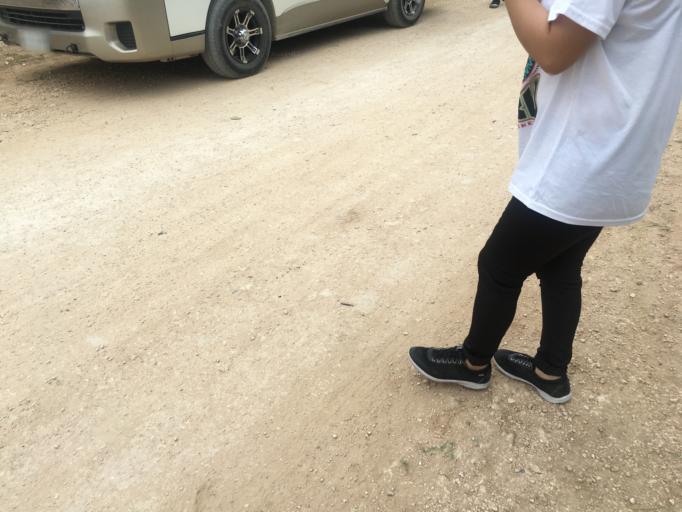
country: PH
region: Davao
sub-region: Province of Davao del Norte
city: San Remigio
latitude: 6.9364
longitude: 125.7788
